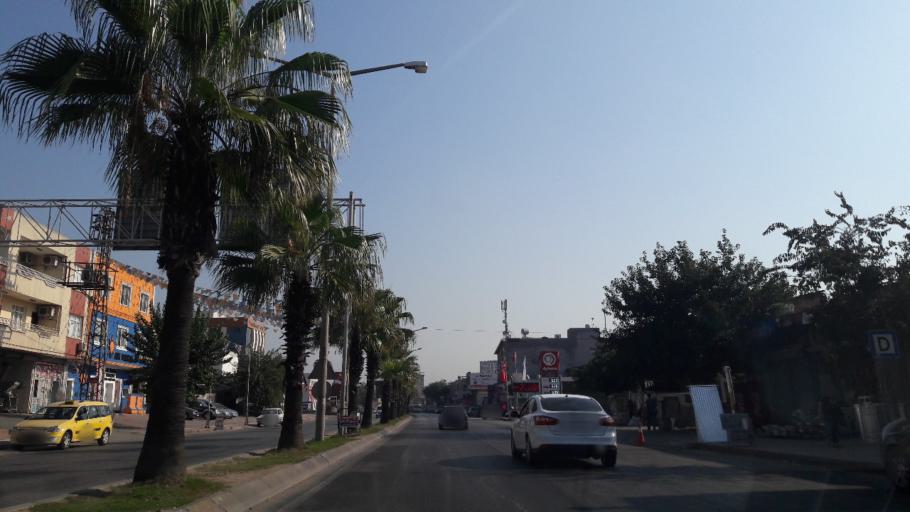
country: TR
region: Adana
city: Yuregir
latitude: 37.0260
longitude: 35.4002
